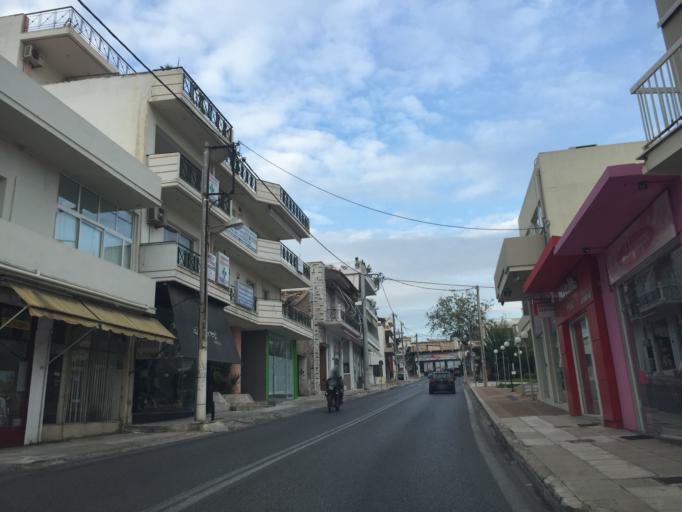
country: GR
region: Attica
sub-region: Nomarchia Anatolikis Attikis
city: Vari
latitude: 37.8315
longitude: 23.8026
